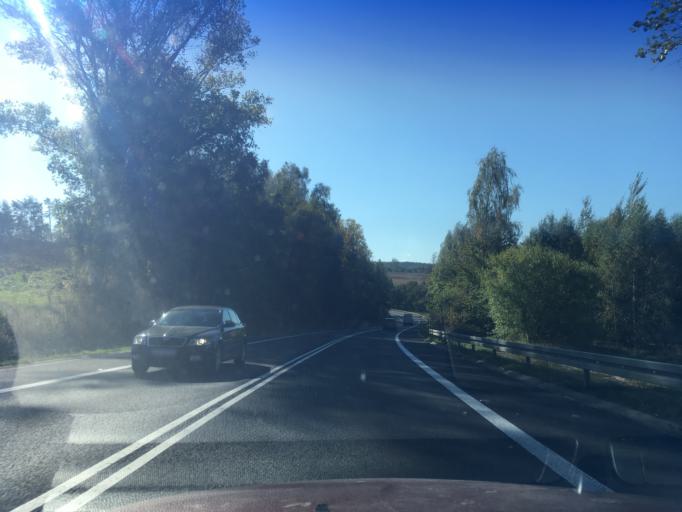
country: DE
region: Saxony
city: Ostritz
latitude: 50.9969
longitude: 14.9444
